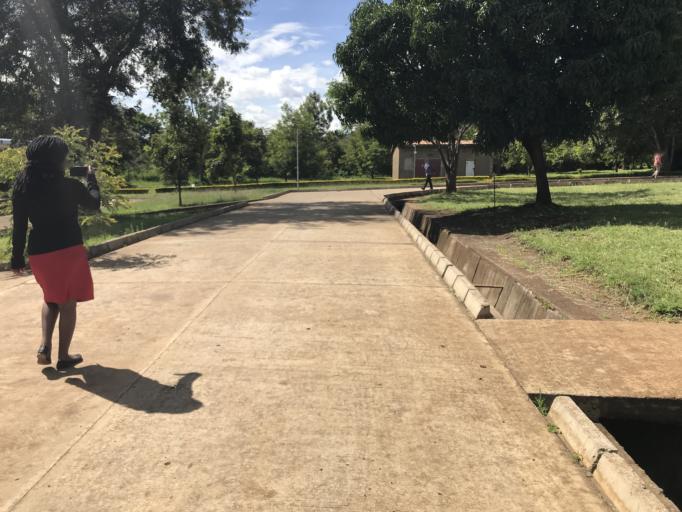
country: TZ
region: Arusha
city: Usa River
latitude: -3.4008
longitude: 36.7959
